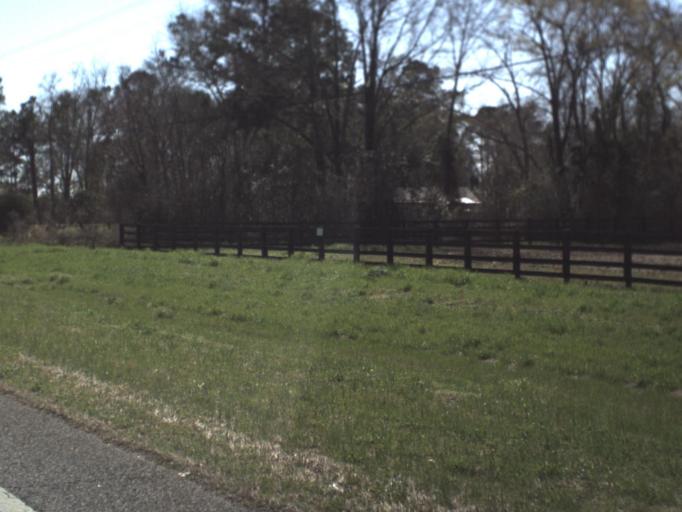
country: US
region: Florida
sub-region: Jackson County
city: Graceville
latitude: 30.9322
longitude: -85.3881
